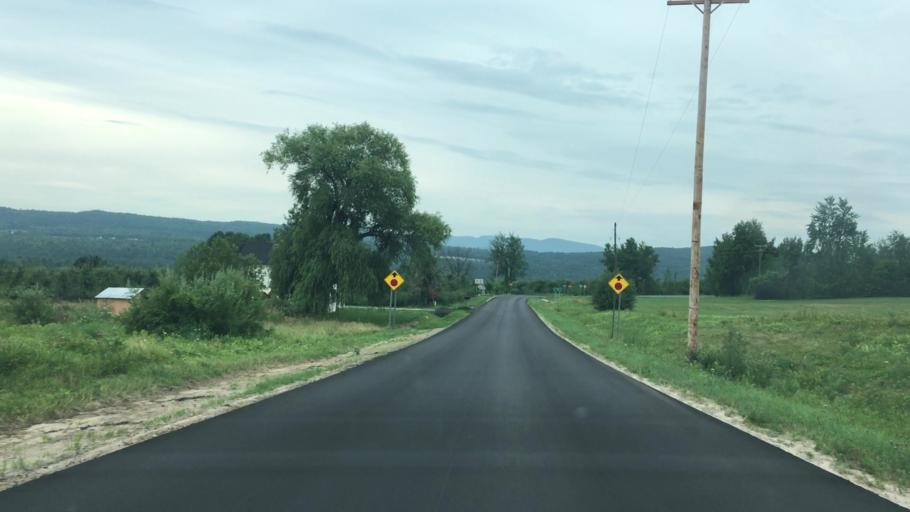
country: US
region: New York
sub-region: Clinton County
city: Peru
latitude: 44.5471
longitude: -73.5642
